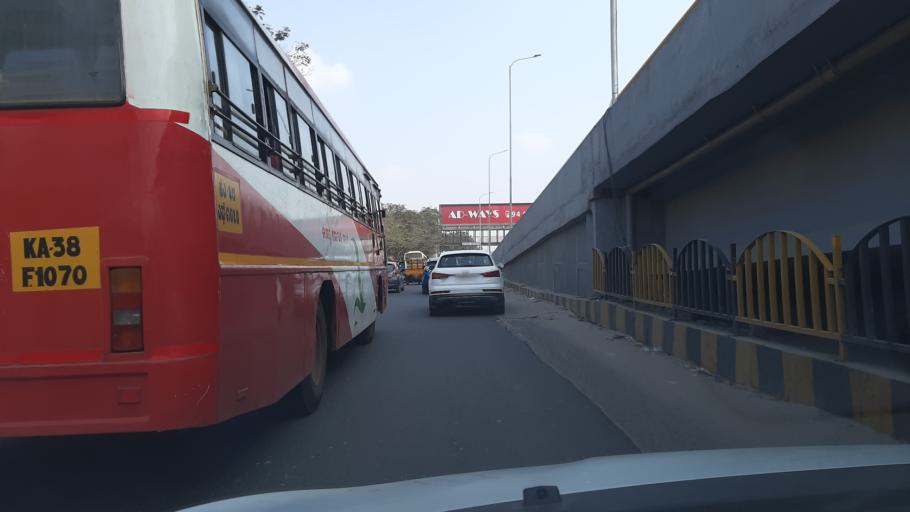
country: IN
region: Telangana
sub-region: Rangareddi
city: Kukatpalli
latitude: 17.4258
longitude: 78.3781
